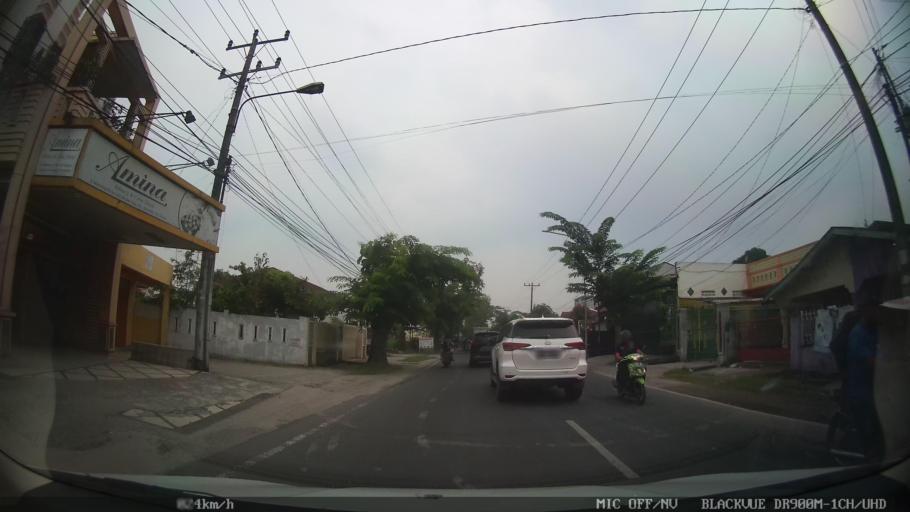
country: ID
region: North Sumatra
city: Medan
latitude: 3.5649
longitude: 98.7224
